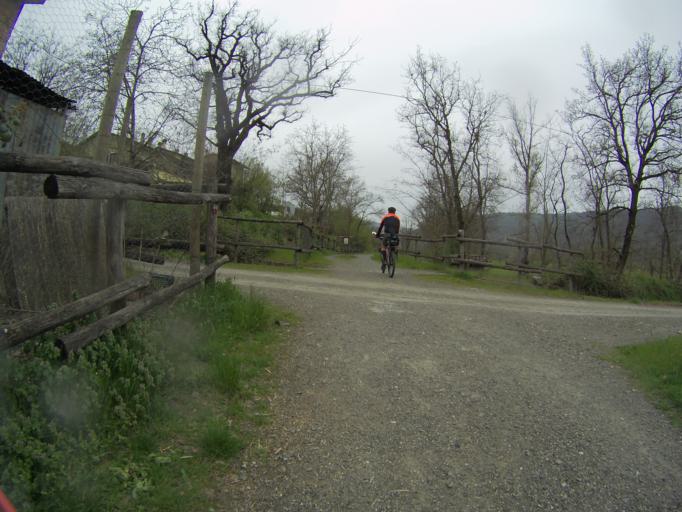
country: IT
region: Emilia-Romagna
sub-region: Provincia di Reggio Emilia
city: Ciano d'Enza
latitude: 44.5856
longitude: 10.4050
